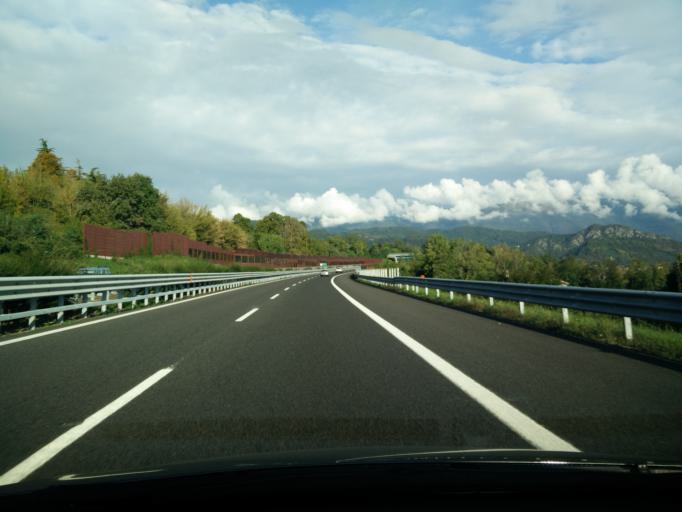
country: IT
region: Veneto
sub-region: Provincia di Treviso
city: Carpesica
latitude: 45.9512
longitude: 12.2956
